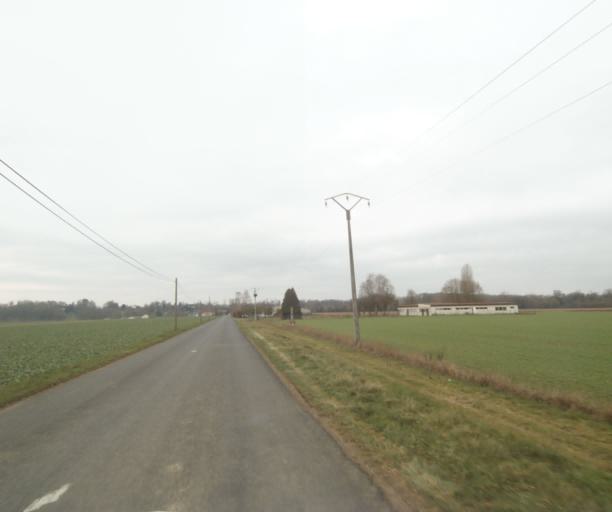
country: FR
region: Champagne-Ardenne
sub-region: Departement de la Haute-Marne
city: Villiers-en-Lieu
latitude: 48.6374
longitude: 4.8653
